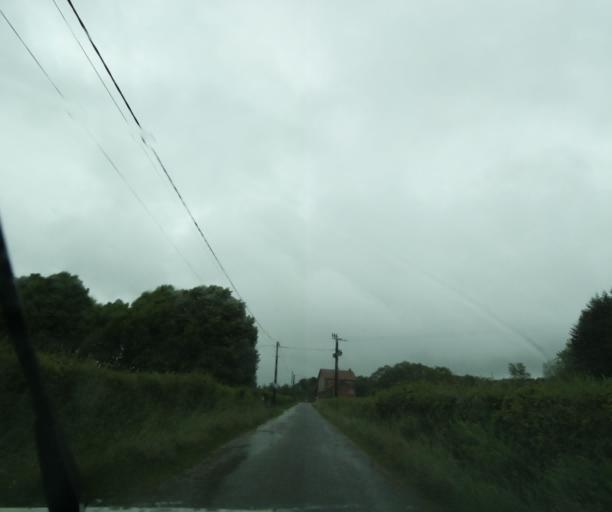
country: FR
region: Bourgogne
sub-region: Departement de Saone-et-Loire
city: Ciry-le-Noble
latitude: 46.5254
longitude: 4.3011
